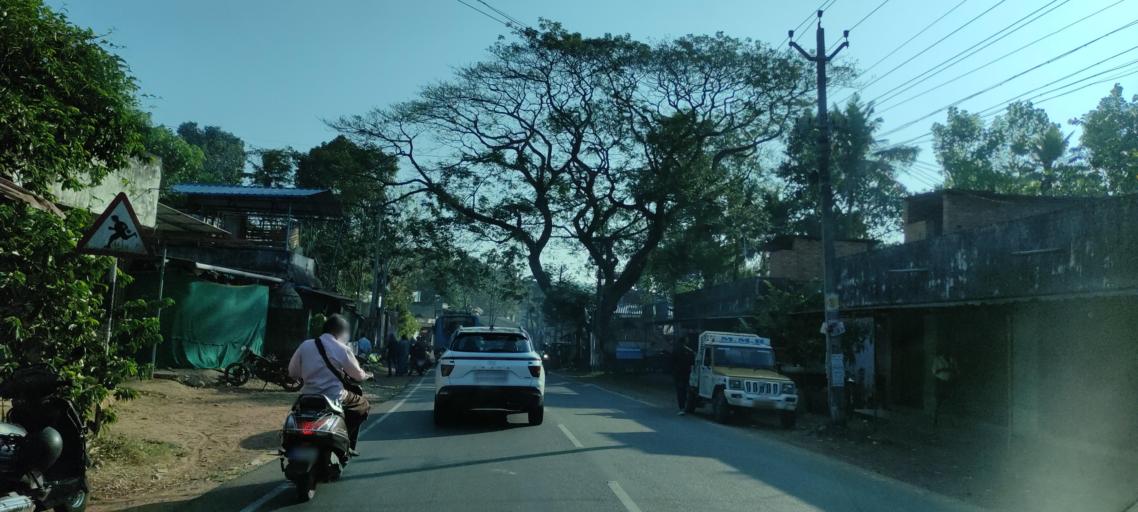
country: IN
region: Kerala
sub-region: Pattanamtitta
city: Adur
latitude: 9.1666
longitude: 76.6693
